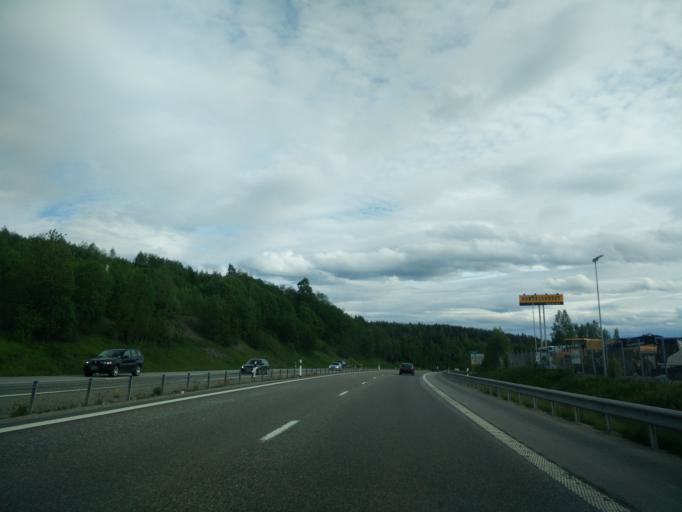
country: SE
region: Vaesternorrland
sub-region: Sundsvalls Kommun
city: Johannedal
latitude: 62.4269
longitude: 17.3487
